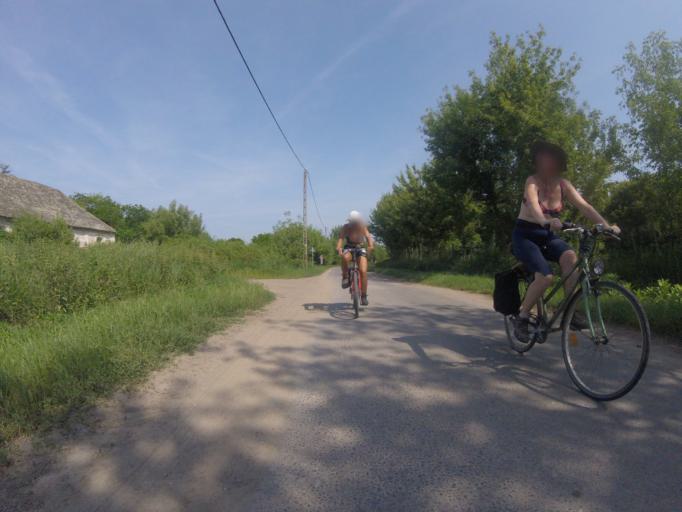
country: HU
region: Tolna
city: Bolcske
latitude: 46.7331
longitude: 18.9235
